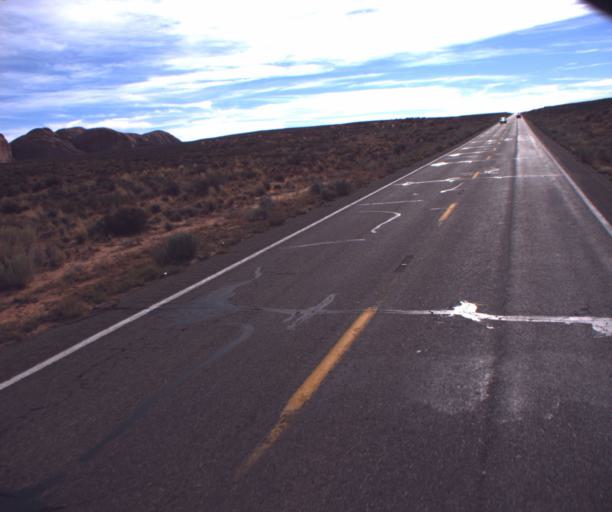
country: US
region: Arizona
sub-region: Coconino County
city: LeChee
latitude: 36.8402
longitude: -111.3248
